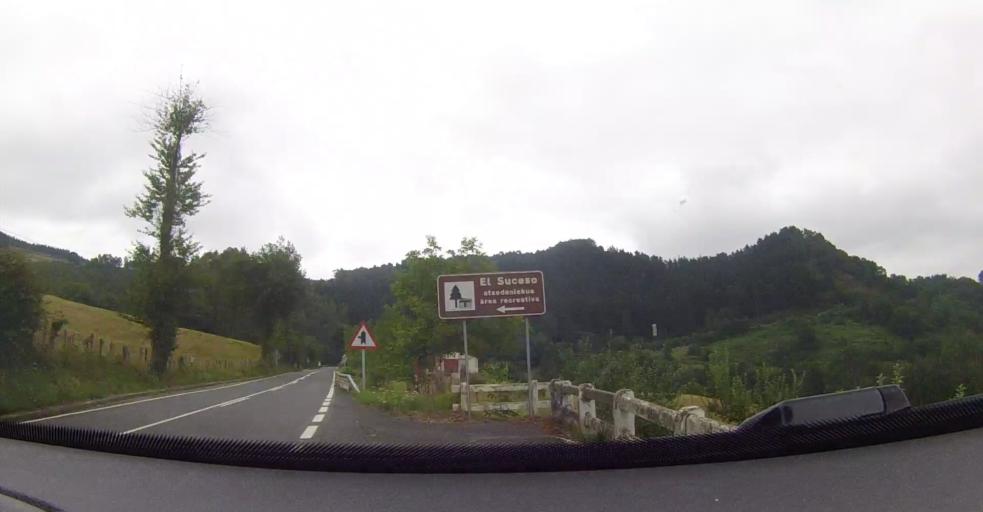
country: ES
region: Basque Country
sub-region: Bizkaia
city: Balmaseda
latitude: 43.2421
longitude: -3.3047
